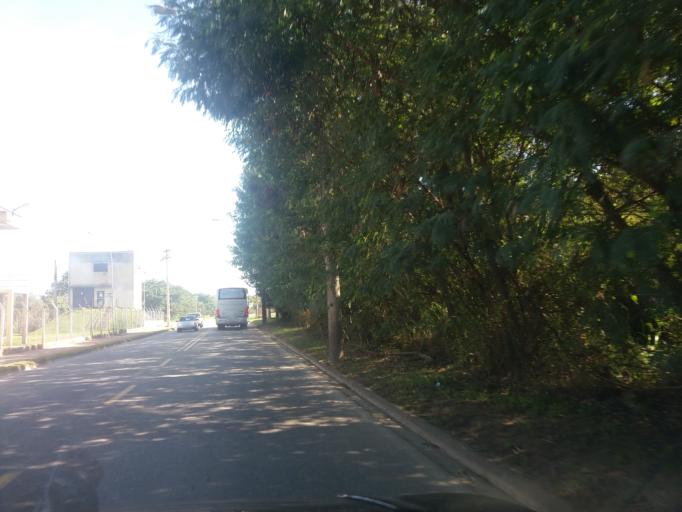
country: BR
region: Sao Paulo
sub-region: Sorocaba
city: Sorocaba
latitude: -23.4690
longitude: -47.4489
